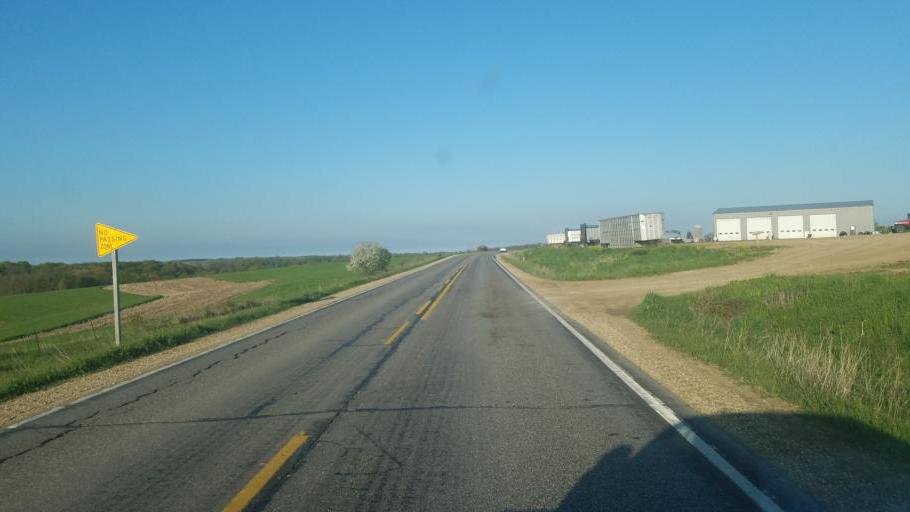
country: US
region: Wisconsin
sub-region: Vernon County
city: Hillsboro
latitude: 43.5965
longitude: -90.4790
